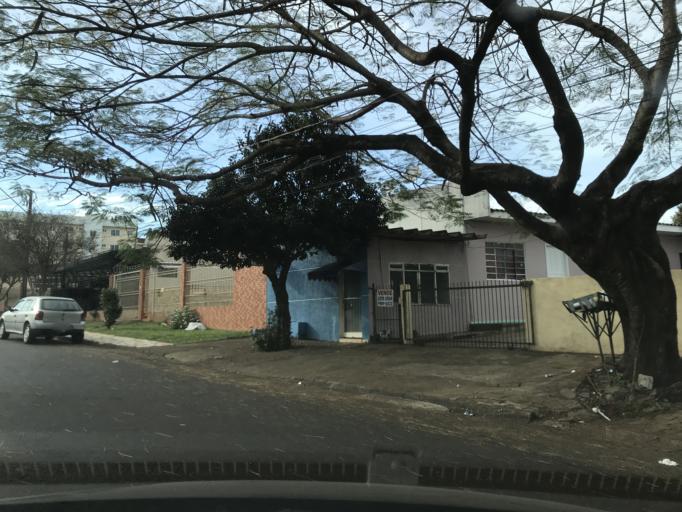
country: BR
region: Parana
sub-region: Cascavel
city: Cascavel
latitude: -24.9563
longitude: -53.4817
